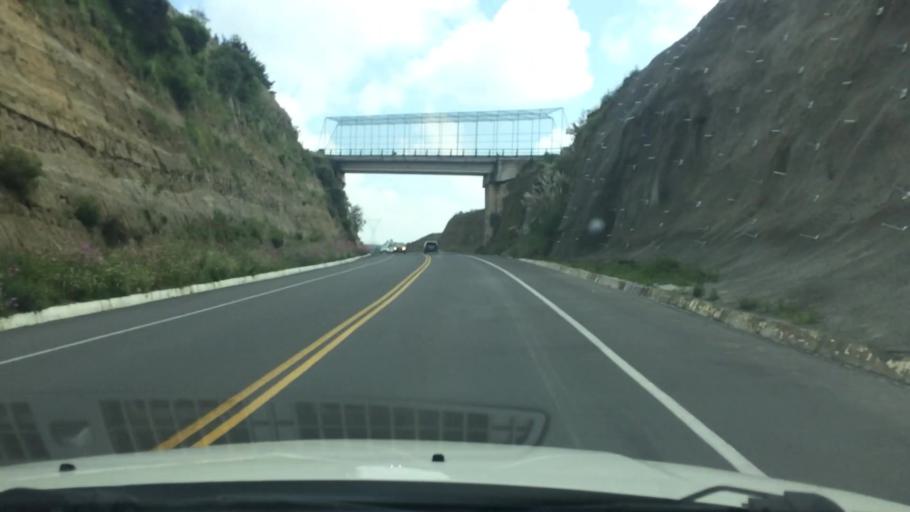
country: MX
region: Mexico
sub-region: Villa Victoria
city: Colonia Doctor Gustavo Baz
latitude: 19.3635
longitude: -99.9462
